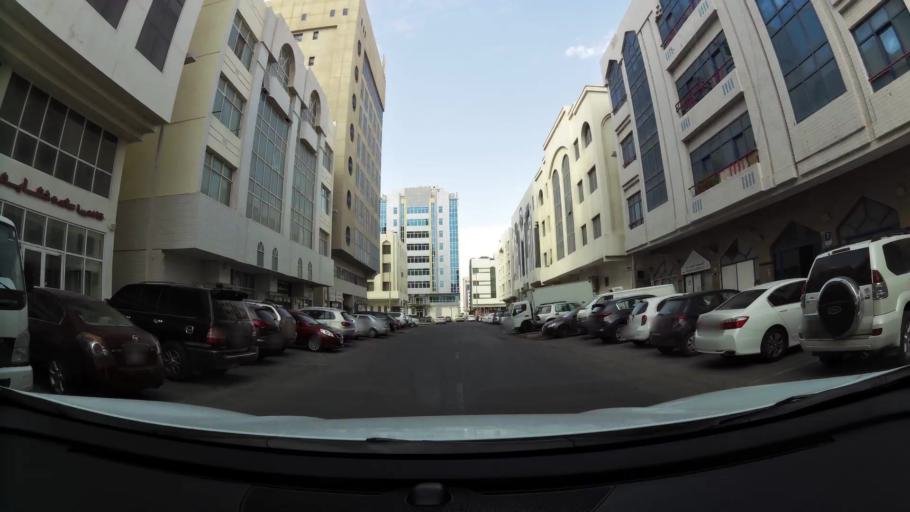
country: AE
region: Abu Dhabi
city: Abu Dhabi
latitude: 24.3233
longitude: 54.5384
